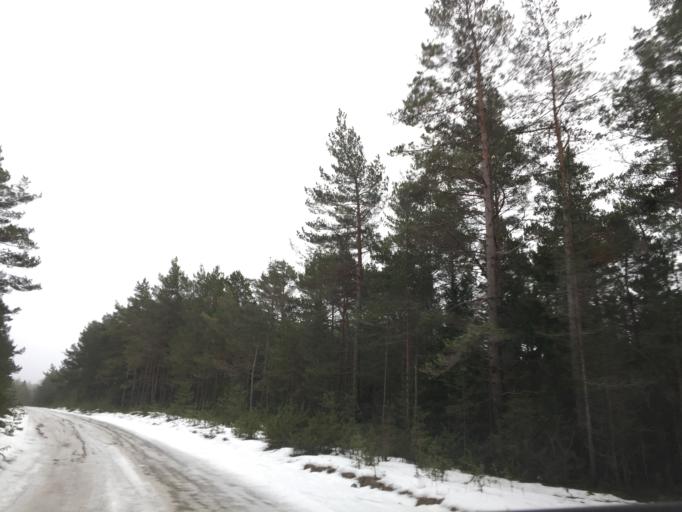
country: EE
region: Saare
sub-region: Kuressaare linn
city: Kuressaare
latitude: 58.5017
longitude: 21.9739
